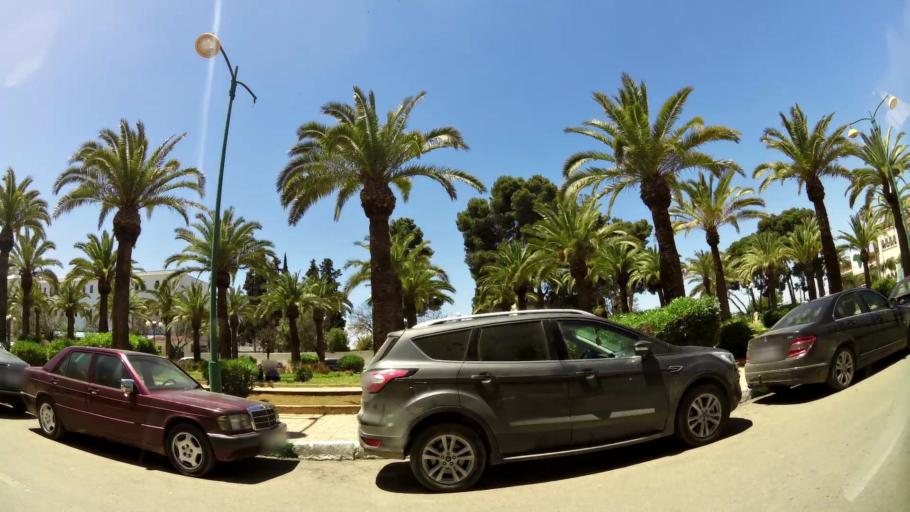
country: MA
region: Meknes-Tafilalet
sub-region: Meknes
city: Meknes
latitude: 33.9057
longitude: -5.5525
